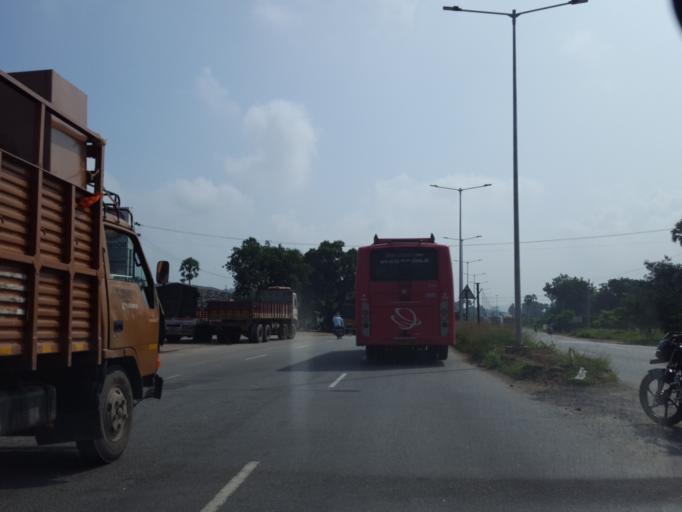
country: IN
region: Telangana
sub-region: Rangareddi
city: Ghatkesar
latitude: 17.3069
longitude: 78.7091
